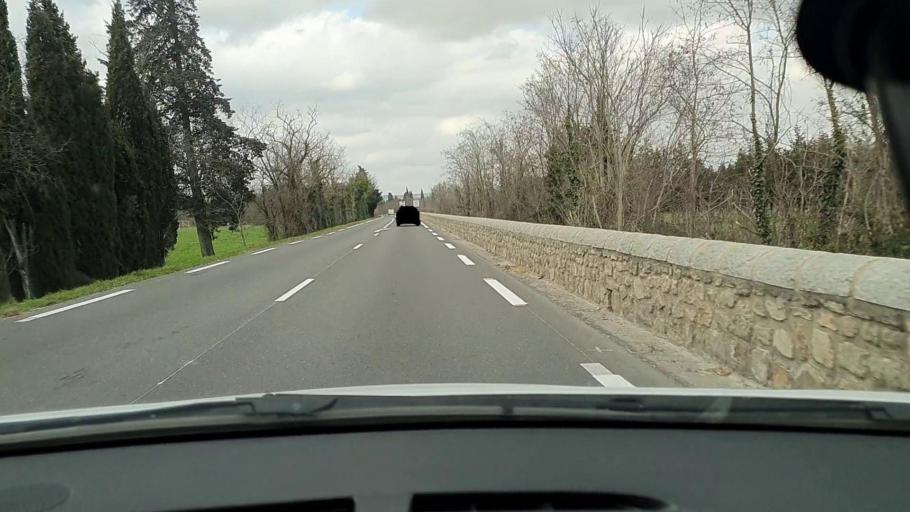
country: FR
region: Languedoc-Roussillon
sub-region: Departement du Gard
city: Meynes
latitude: 43.8767
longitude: 4.5789
